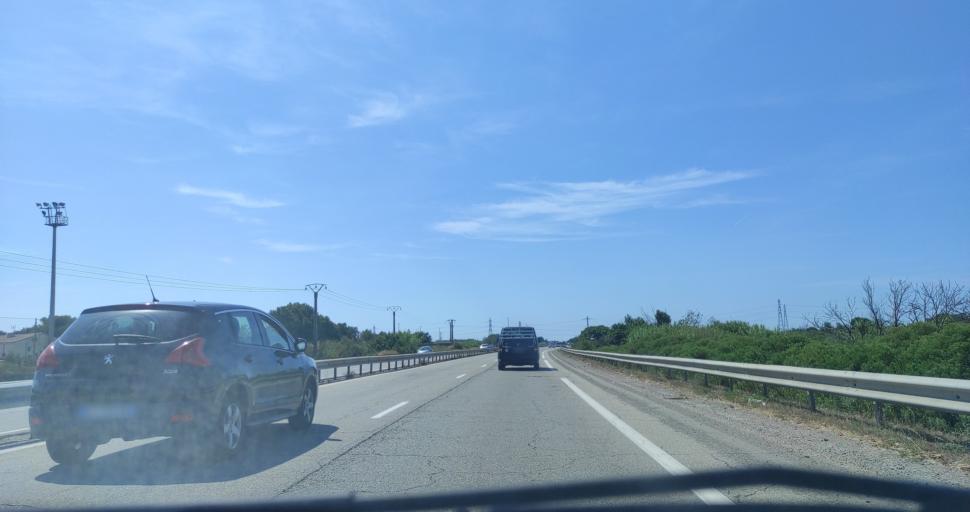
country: FR
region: Provence-Alpes-Cote d'Azur
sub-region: Departement des Bouches-du-Rhone
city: Fos-sur-Mer
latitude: 43.4436
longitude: 4.9394
